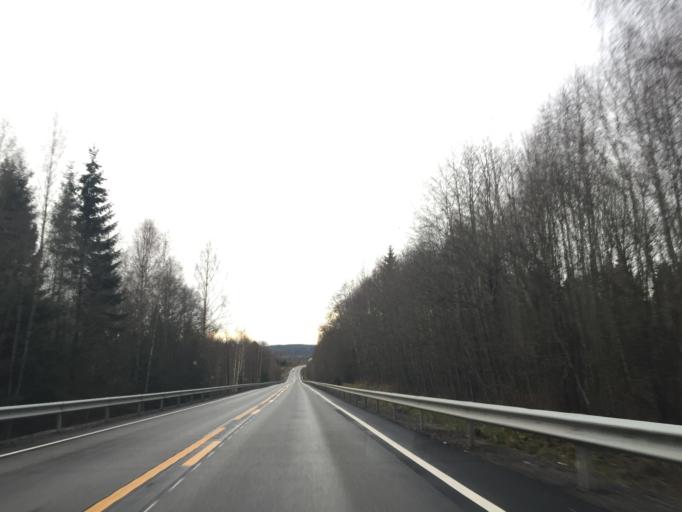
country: NO
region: Hedmark
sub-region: Asnes
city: Flisa
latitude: 60.6176
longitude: 11.9766
